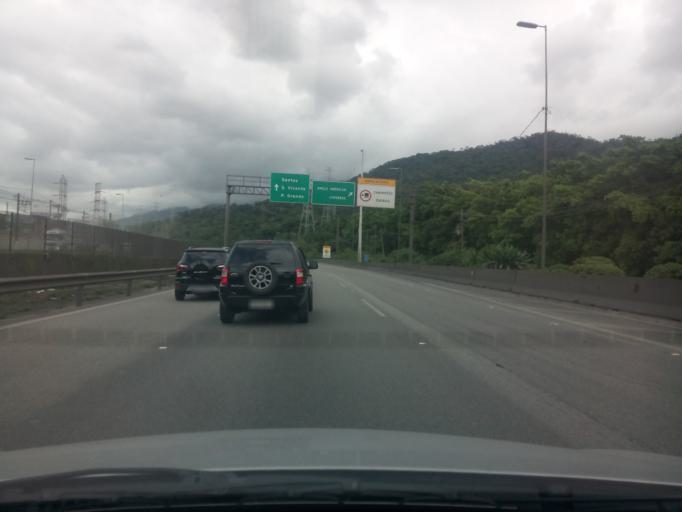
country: BR
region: Sao Paulo
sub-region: Cubatao
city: Cubatao
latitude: -23.8467
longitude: -46.3971
